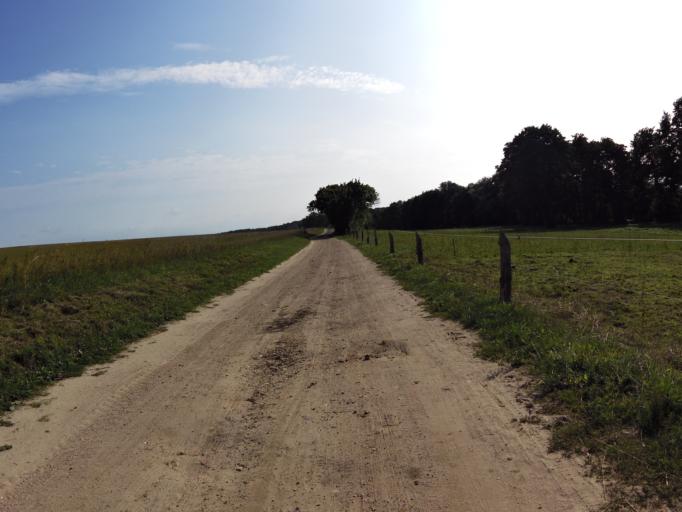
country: DE
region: Mecklenburg-Vorpommern
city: Seebad Bansin
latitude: 53.9544
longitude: 14.1424
